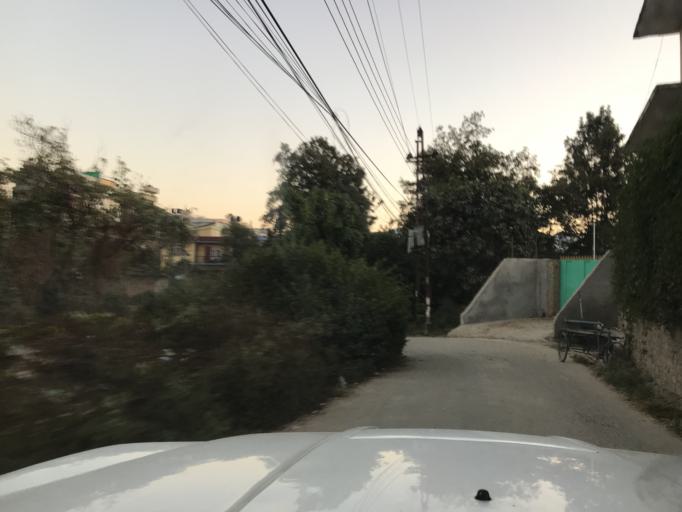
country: NP
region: Central Region
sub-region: Bagmati Zone
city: Patan
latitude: 27.6487
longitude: 85.3158
